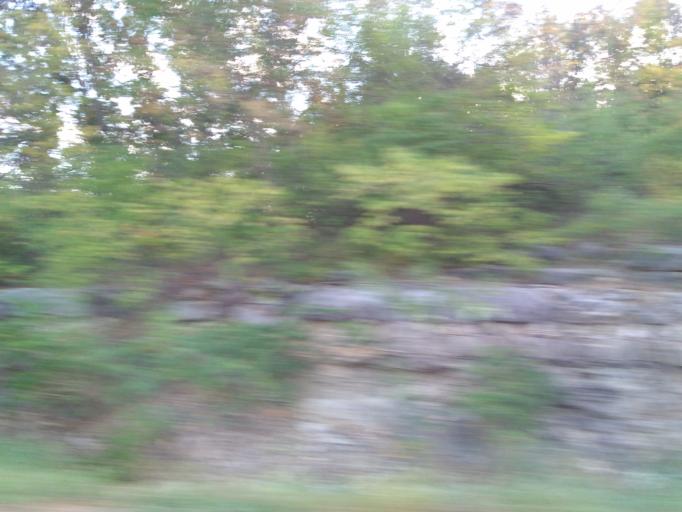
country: US
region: Missouri
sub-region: Saint Louis County
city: Concord
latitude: 38.5135
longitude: -90.3742
